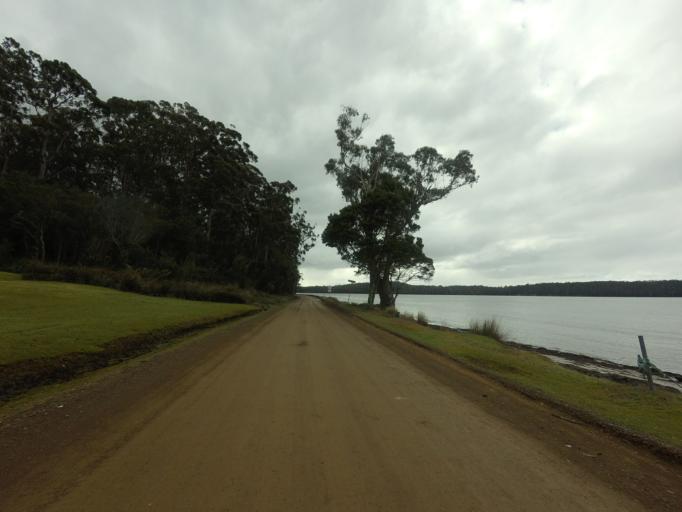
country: AU
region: Tasmania
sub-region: Huon Valley
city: Geeveston
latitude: -43.5333
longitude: 146.8918
